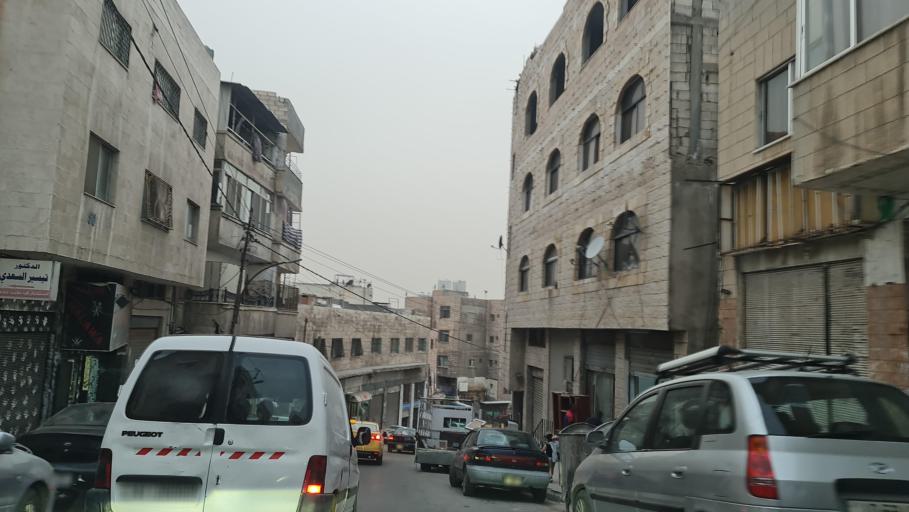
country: JO
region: Amman
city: Amman
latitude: 31.9459
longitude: 35.9443
